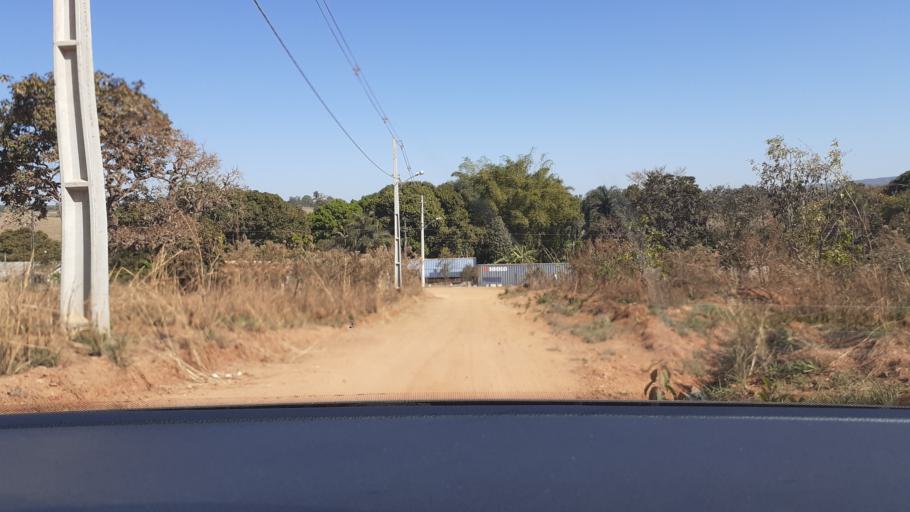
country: BR
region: Goias
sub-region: Aparecida De Goiania
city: Aparecida de Goiania
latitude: -16.8911
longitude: -49.2612
